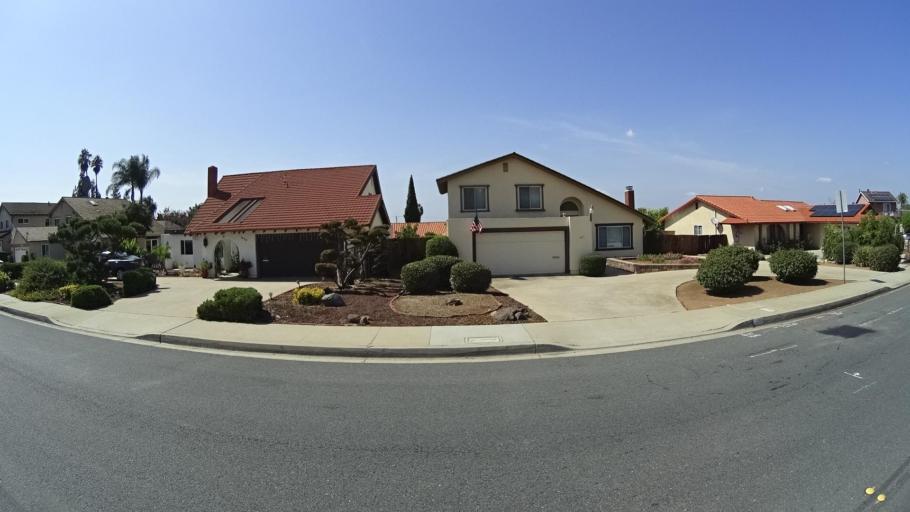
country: US
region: California
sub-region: San Diego County
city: Granite Hills
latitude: 32.7869
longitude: -116.9178
